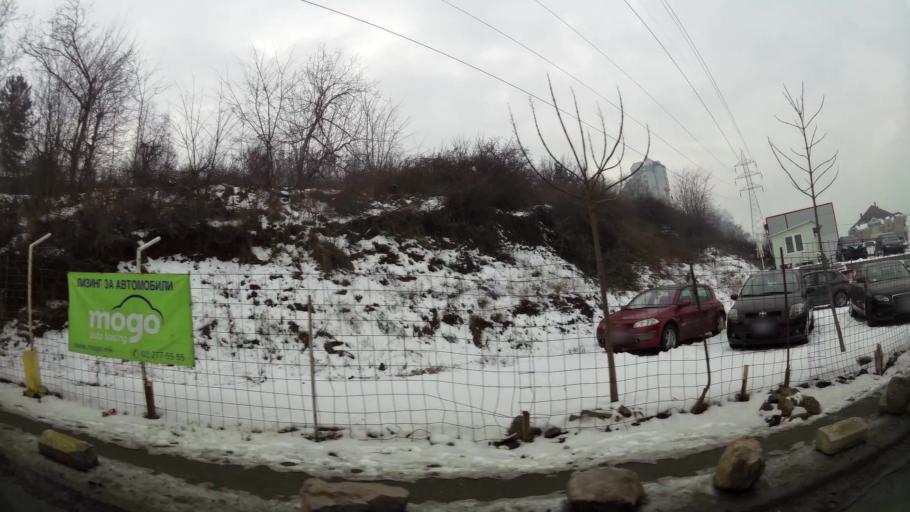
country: MK
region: Cair
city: Cair
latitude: 42.0170
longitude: 21.4538
